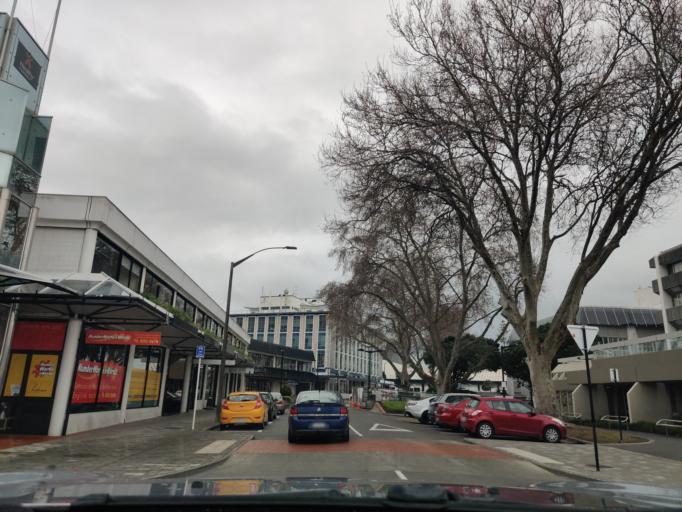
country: NZ
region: Hawke's Bay
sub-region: Napier City
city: Napier
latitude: -39.4925
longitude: 176.9167
